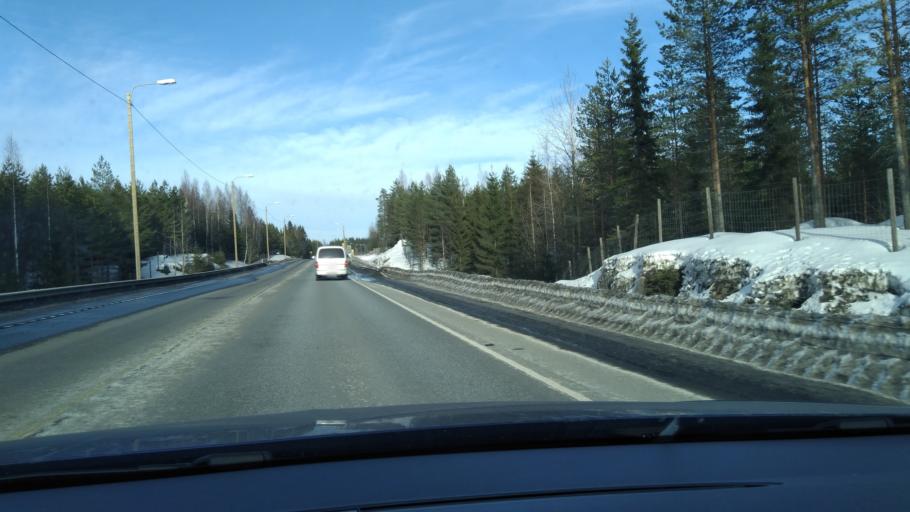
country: FI
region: Pirkanmaa
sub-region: Tampere
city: Orivesi
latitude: 61.6674
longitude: 24.2754
